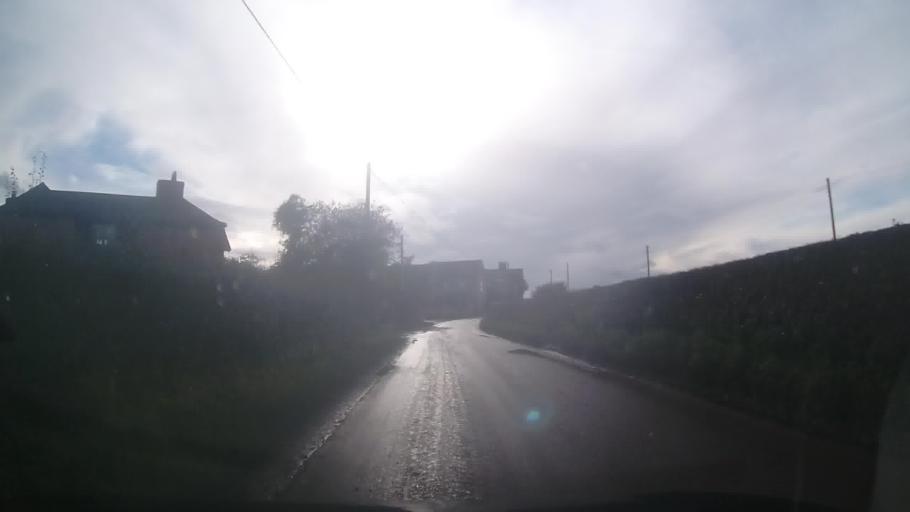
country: GB
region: England
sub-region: Shropshire
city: Whitchurch
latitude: 52.9536
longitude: -2.6968
